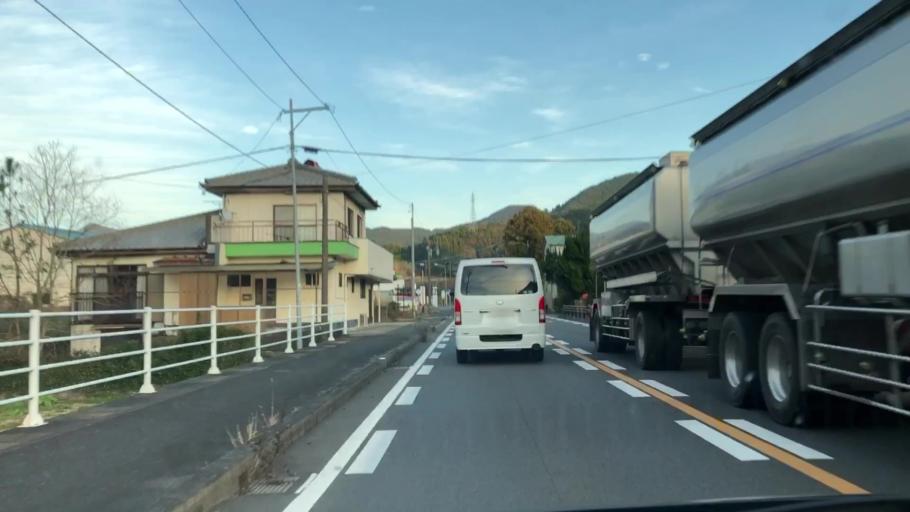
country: JP
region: Kumamoto
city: Minamata
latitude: 32.2314
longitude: 130.4585
